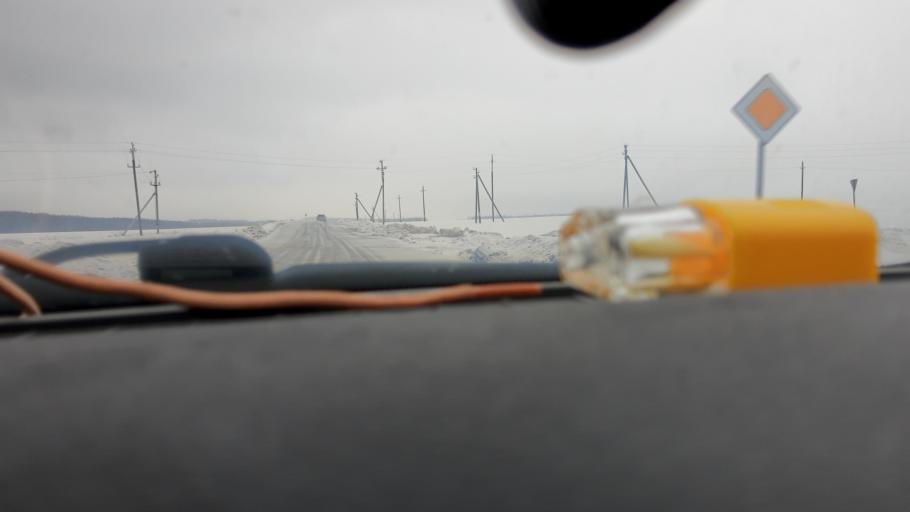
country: RU
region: Bashkortostan
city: Ulukulevo
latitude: 54.6025
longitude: 56.4269
